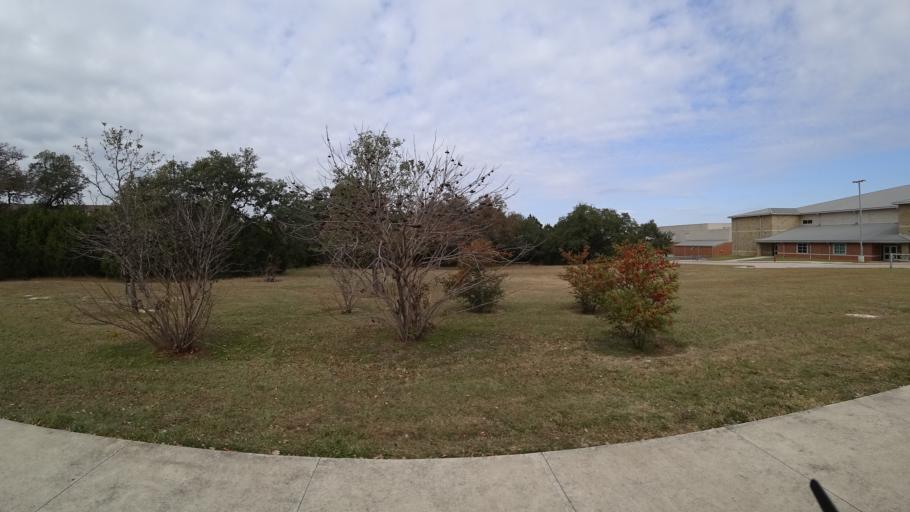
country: US
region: Texas
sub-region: Williamson County
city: Anderson Mill
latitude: 30.3959
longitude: -97.8309
